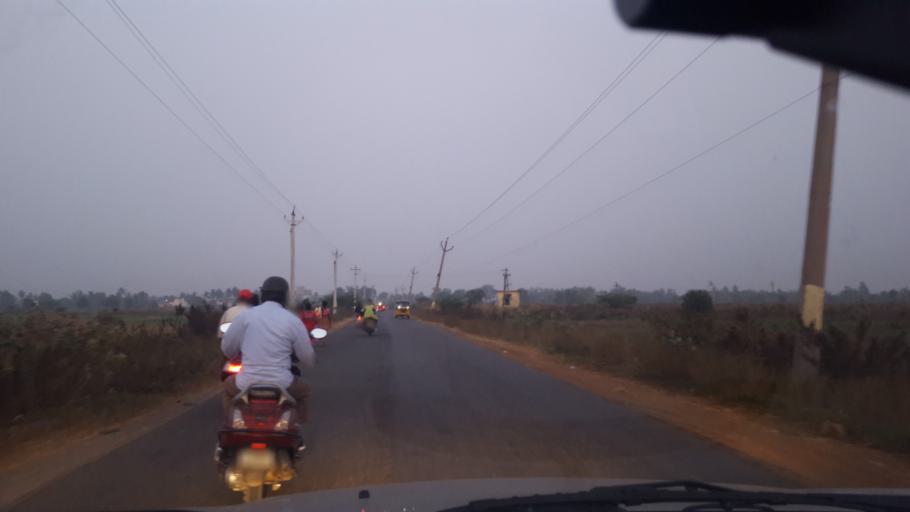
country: IN
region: Andhra Pradesh
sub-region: Srikakulam
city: Palasa
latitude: 18.7304
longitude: 84.3949
